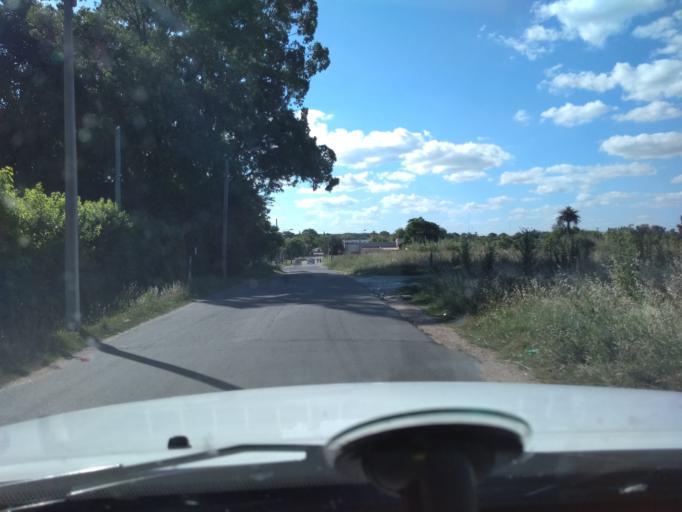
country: UY
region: Canelones
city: La Paz
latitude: -34.8096
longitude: -56.2084
